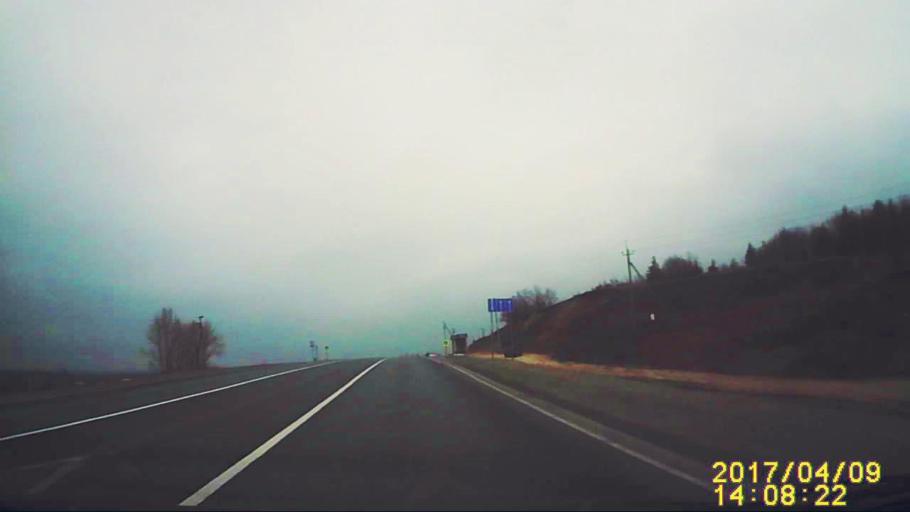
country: RU
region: Ulyanovsk
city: Silikatnyy
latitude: 54.0196
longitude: 48.2156
